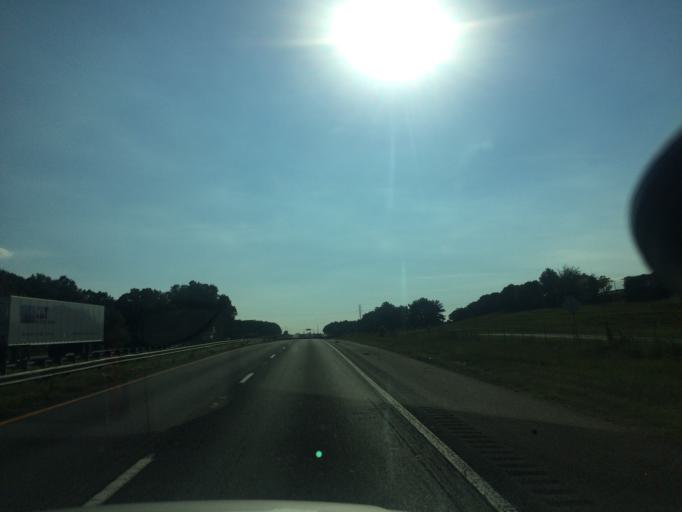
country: US
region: South Carolina
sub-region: Spartanburg County
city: Cowpens
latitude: 35.0324
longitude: -81.8526
